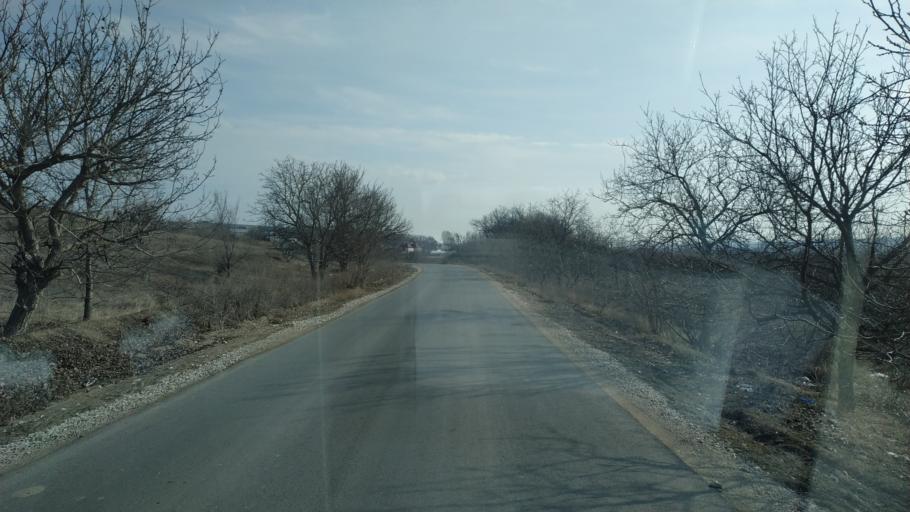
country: MD
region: Chisinau
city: Singera
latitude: 46.9189
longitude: 29.1014
